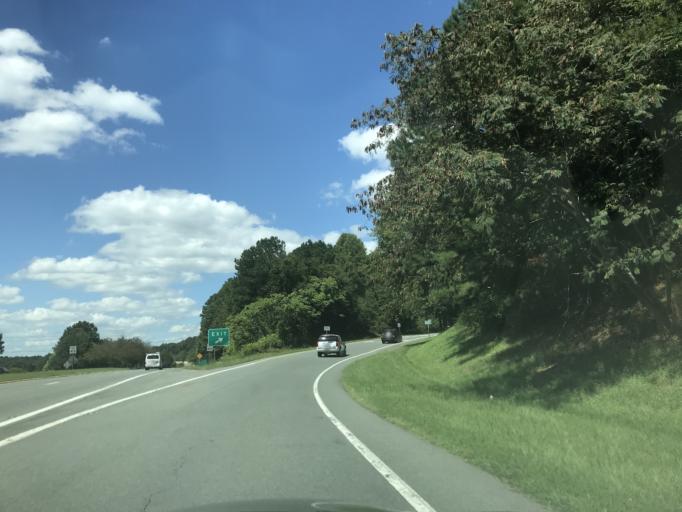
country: US
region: North Carolina
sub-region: Orange County
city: Carrboro
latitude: 35.9002
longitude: -79.0697
